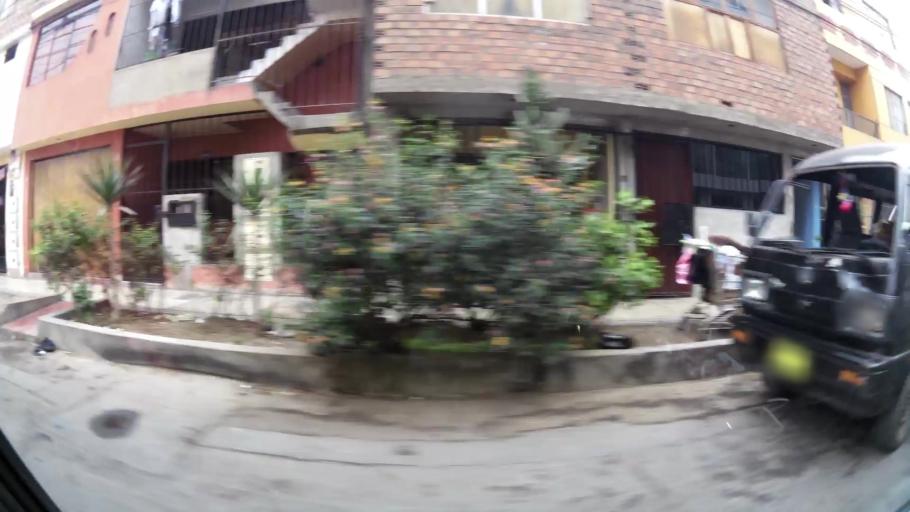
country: PE
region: Lima
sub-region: Lima
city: Independencia
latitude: -11.9725
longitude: -77.0708
